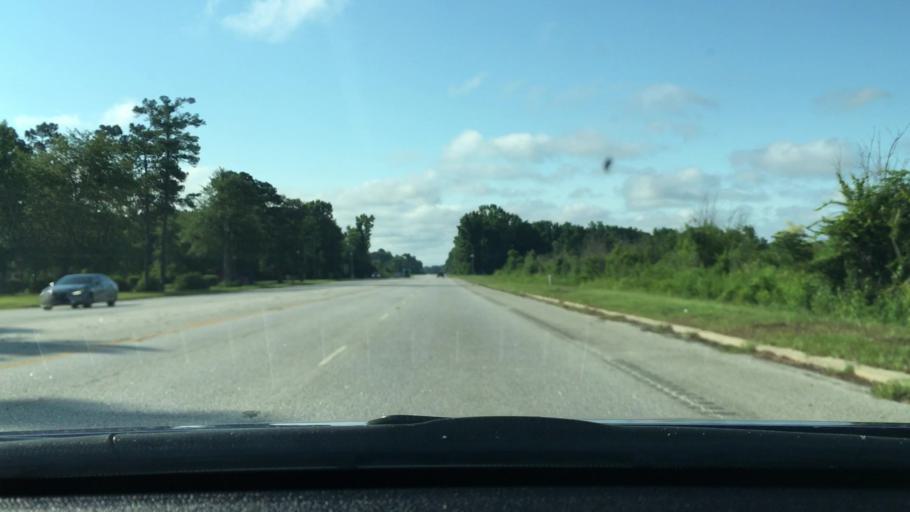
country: US
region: South Carolina
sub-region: Clarendon County
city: Manning
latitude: 33.7644
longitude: -80.2316
